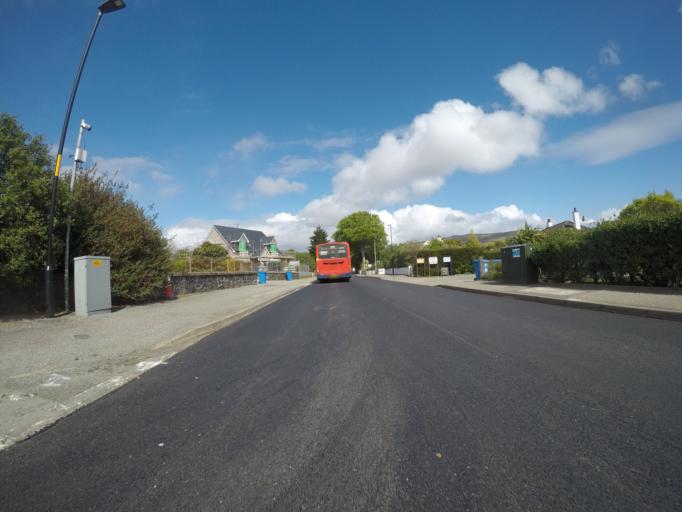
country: GB
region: Scotland
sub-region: Highland
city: Portree
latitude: 57.4101
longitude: -6.2021
